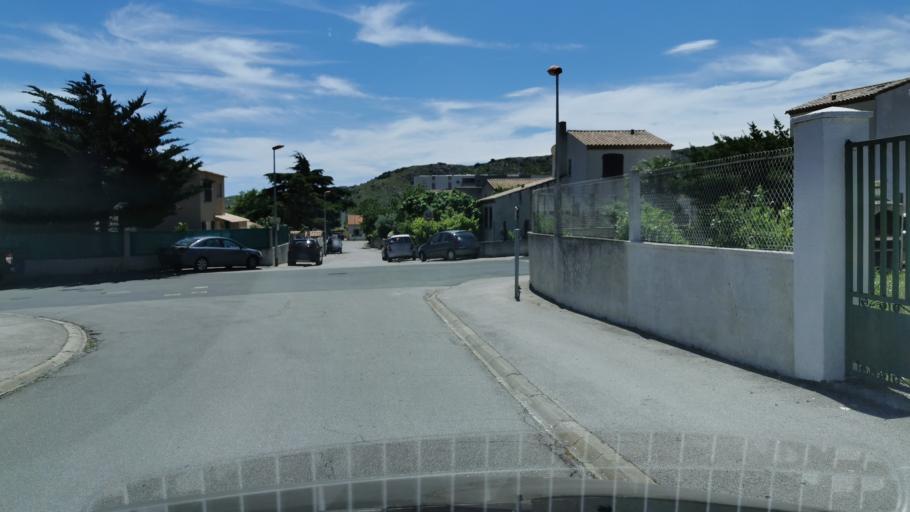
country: FR
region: Languedoc-Roussillon
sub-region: Departement de l'Aude
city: Narbonne
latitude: 43.1830
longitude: 2.9714
